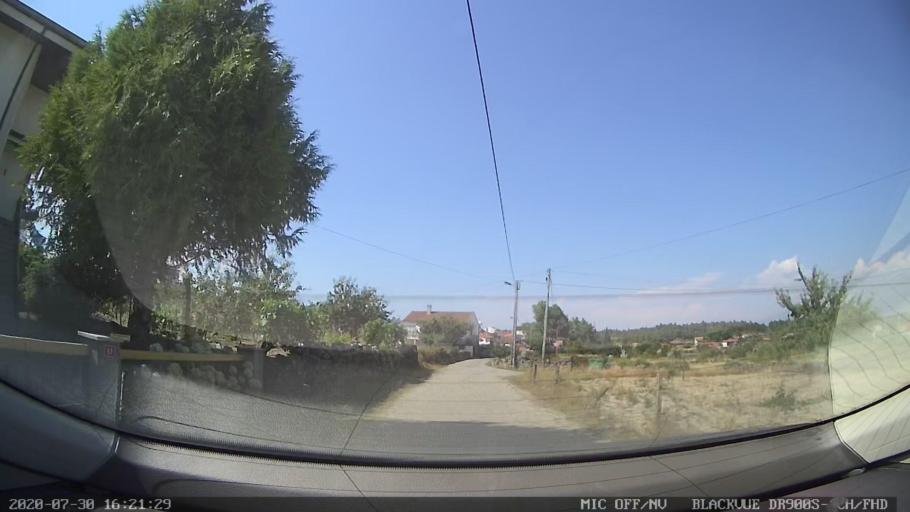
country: PT
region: Vila Real
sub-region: Murca
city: Murca
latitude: 41.3235
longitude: -7.4890
